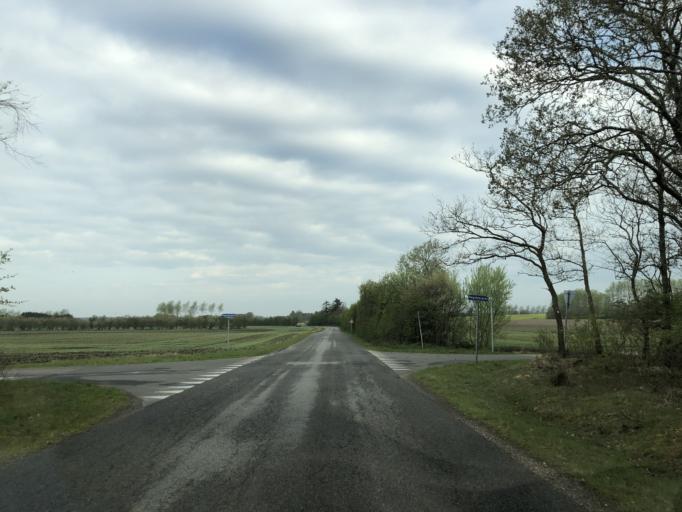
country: DK
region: Central Jutland
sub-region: Holstebro Kommune
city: Holstebro
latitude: 56.3216
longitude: 8.5108
